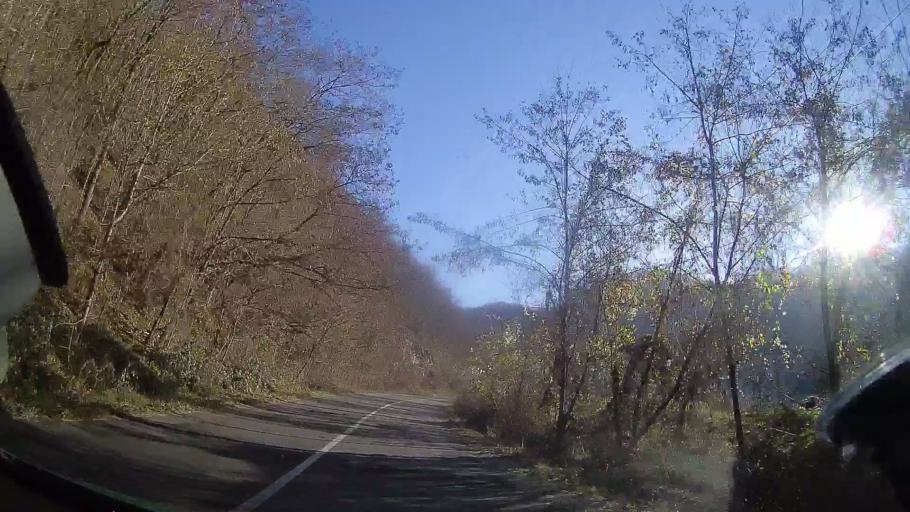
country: RO
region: Bihor
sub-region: Comuna Bulz
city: Bulz
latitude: 46.9169
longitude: 22.6563
